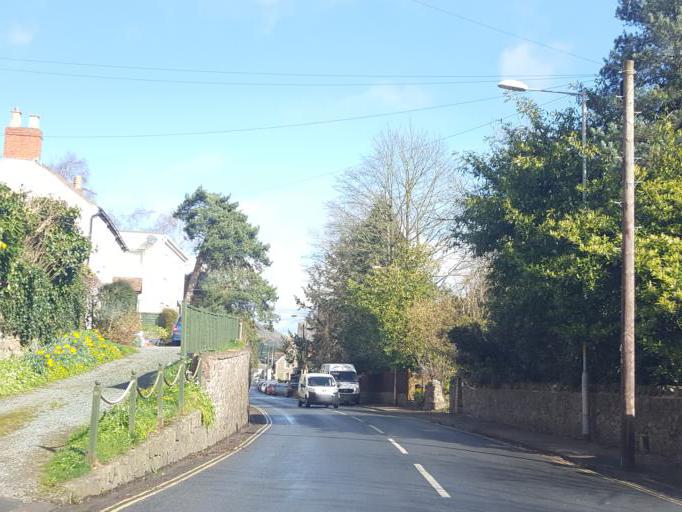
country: GB
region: England
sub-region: Worcestershire
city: Great Malvern
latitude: 52.0758
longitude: -2.3323
